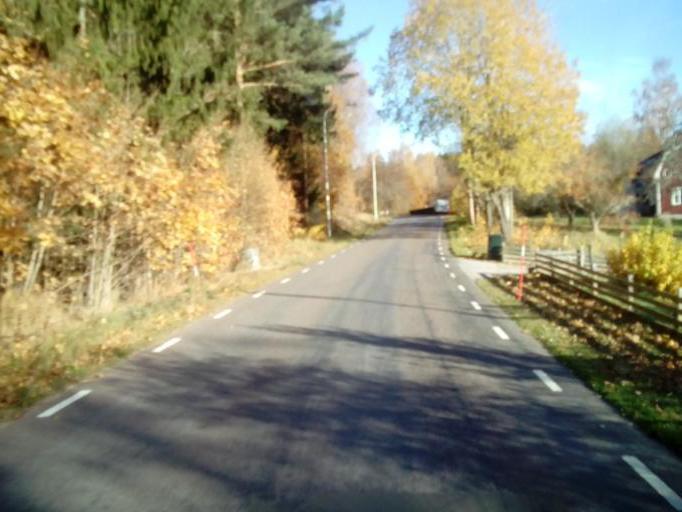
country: SE
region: Kalmar
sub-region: Vimmerby Kommun
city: Vimmerby
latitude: 57.6821
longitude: 15.8873
